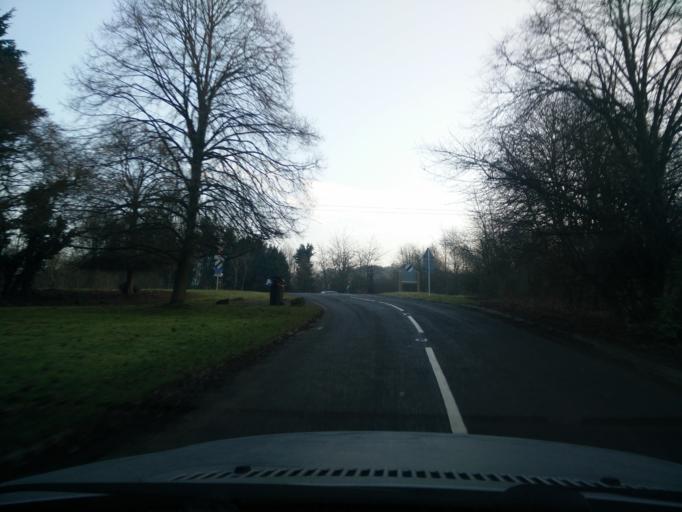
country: GB
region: England
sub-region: Buckinghamshire
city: Amersham
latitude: 51.6814
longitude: -0.6587
